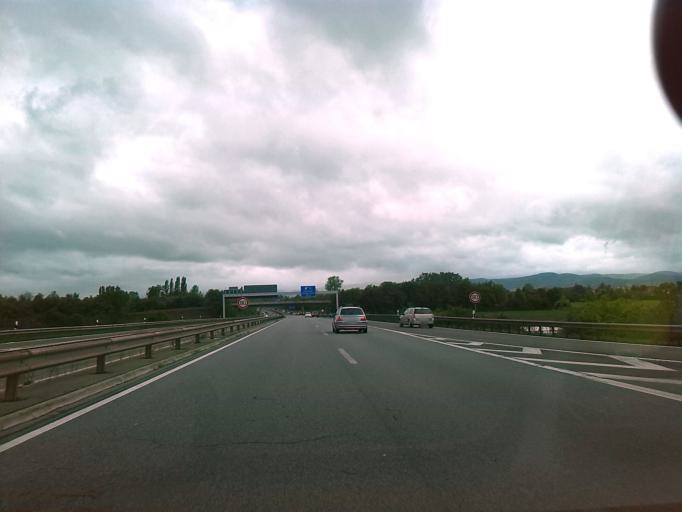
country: DE
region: Rheinland-Pfalz
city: Dannstadt-Schauernheim
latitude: 49.4417
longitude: 8.3210
